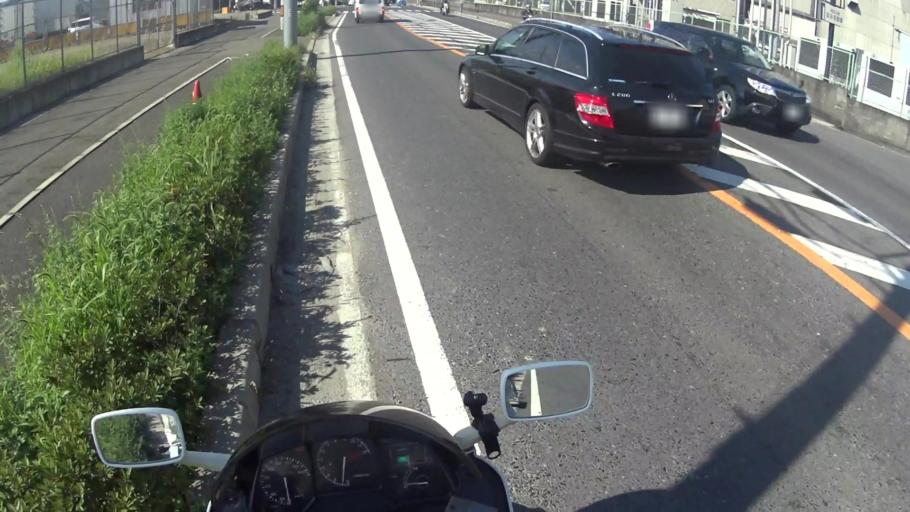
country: JP
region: Kyoto
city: Tanabe
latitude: 34.8492
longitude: 135.7458
